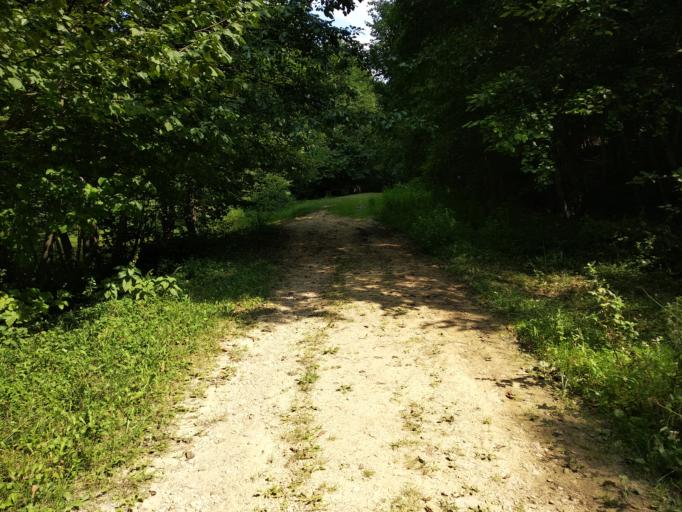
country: RU
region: Adygeya
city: Kamennomostskiy
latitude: 44.1947
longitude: 39.9519
